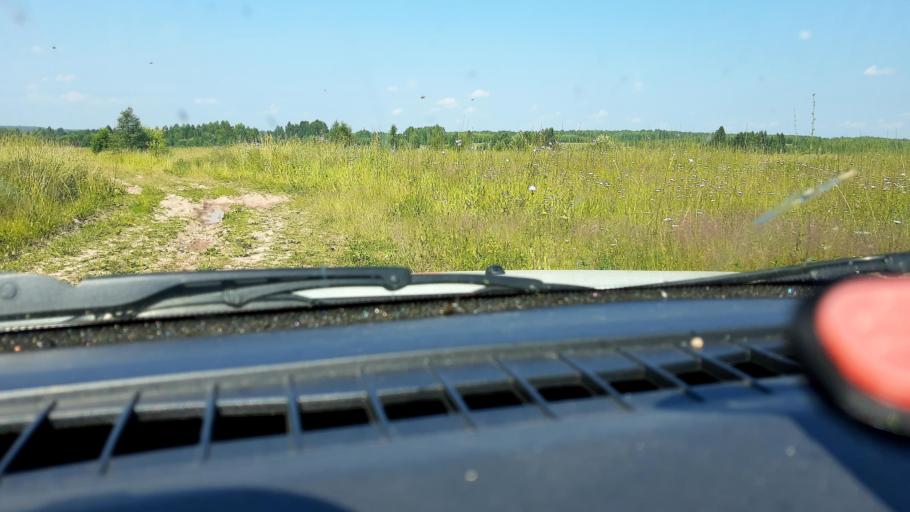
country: RU
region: Nizjnij Novgorod
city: Sharanga
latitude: 57.0470
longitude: 46.7216
